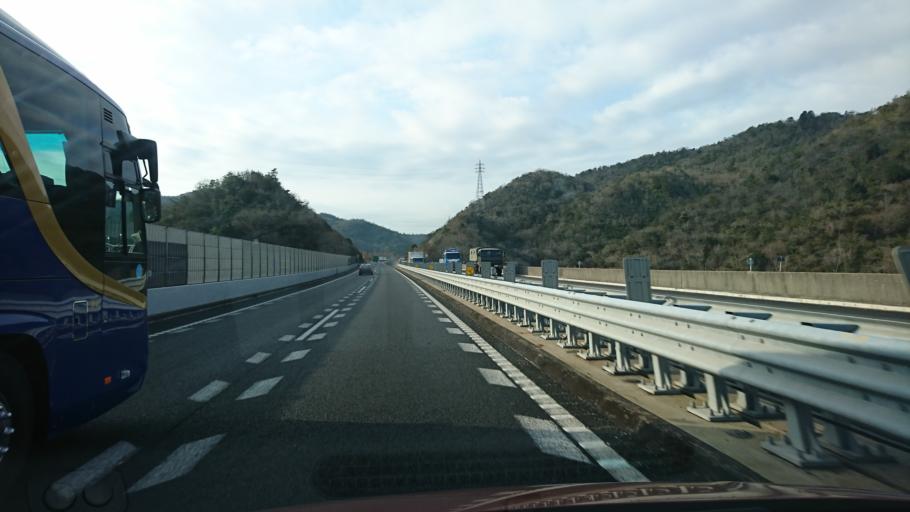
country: JP
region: Hyogo
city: Aioi
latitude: 34.8013
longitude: 134.4367
